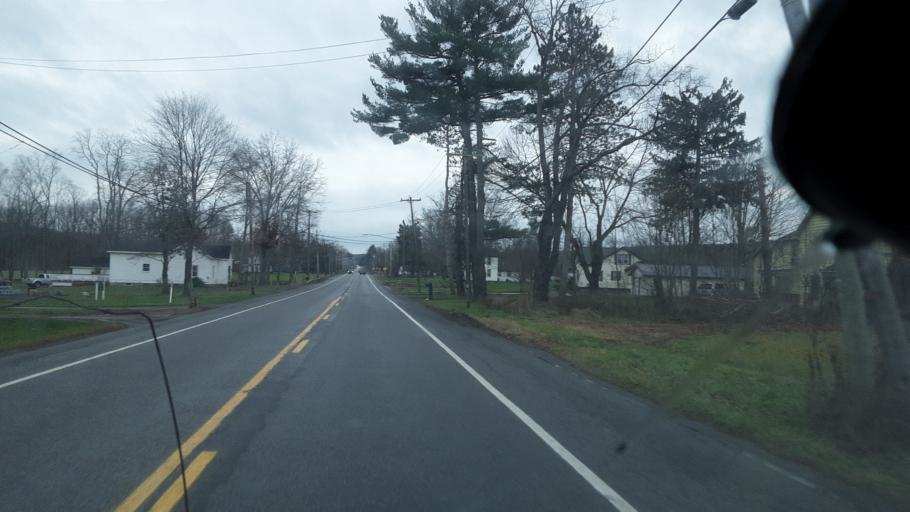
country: US
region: New York
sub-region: Erie County
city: Holland
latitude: 42.6651
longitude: -78.5570
